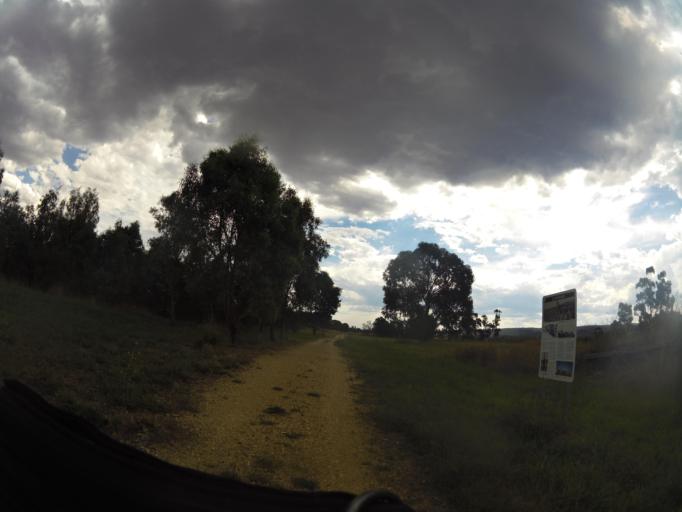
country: AU
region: Victoria
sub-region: Wellington
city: Heyfield
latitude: -38.0151
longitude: 146.6913
